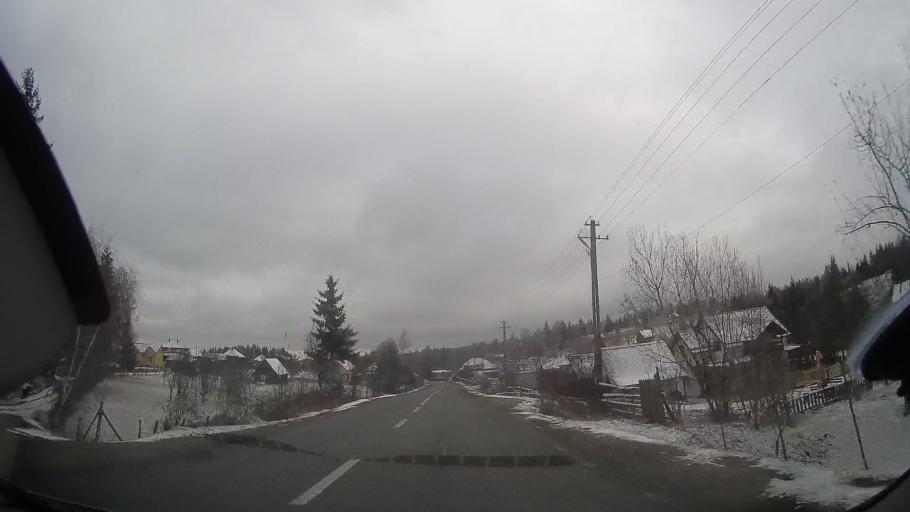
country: RO
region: Cluj
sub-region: Comuna Belis
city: Belis
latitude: 46.7098
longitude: 23.0400
